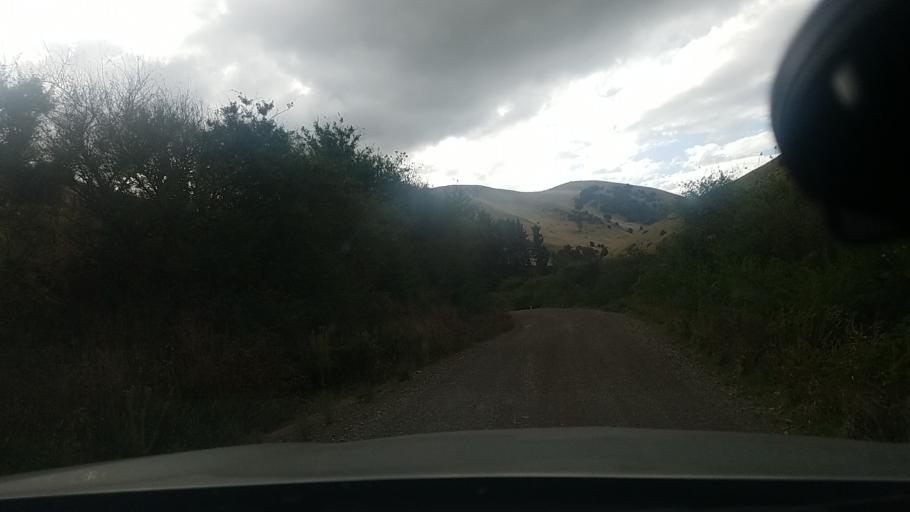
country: NZ
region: Marlborough
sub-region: Marlborough District
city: Blenheim
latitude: -41.5823
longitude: 174.0645
